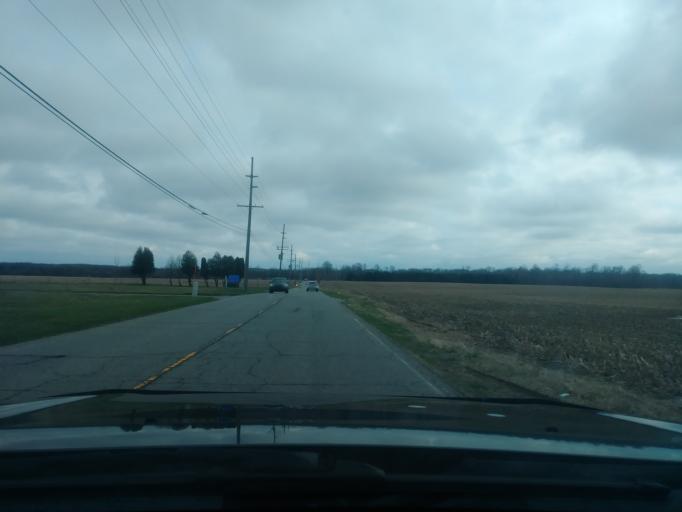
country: US
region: Indiana
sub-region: LaPorte County
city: LaPorte
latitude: 41.6419
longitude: -86.7987
